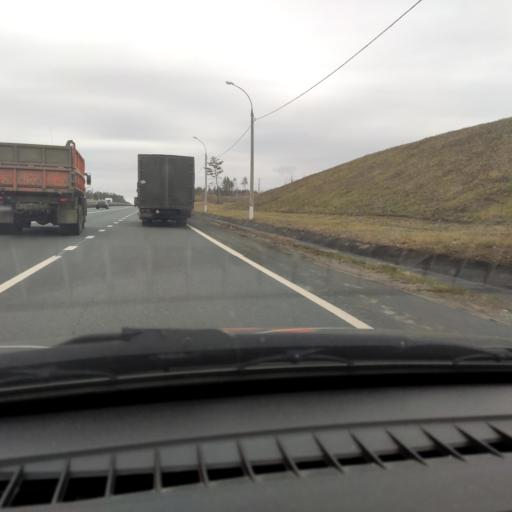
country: RU
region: Samara
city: Zhigulevsk
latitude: 53.4994
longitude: 49.5405
